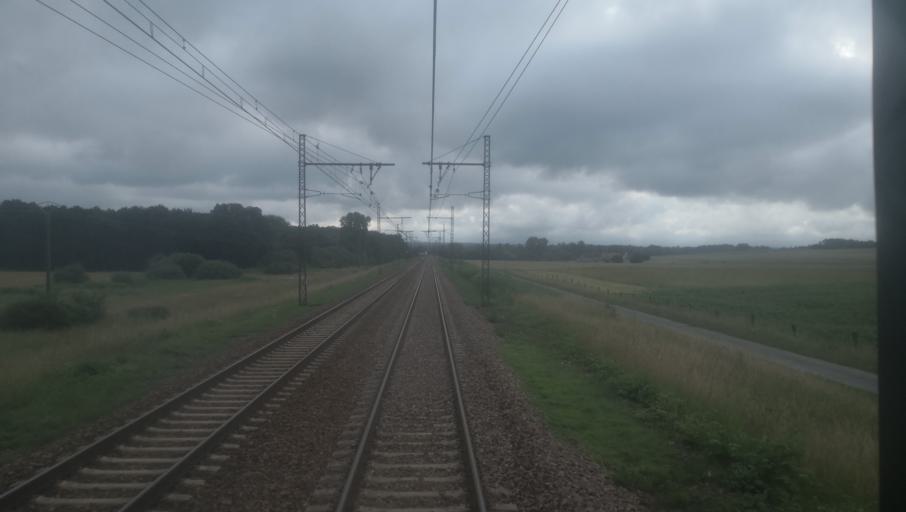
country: FR
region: Centre
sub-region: Departement du Cher
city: Vierzon
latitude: 47.1937
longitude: 2.0822
